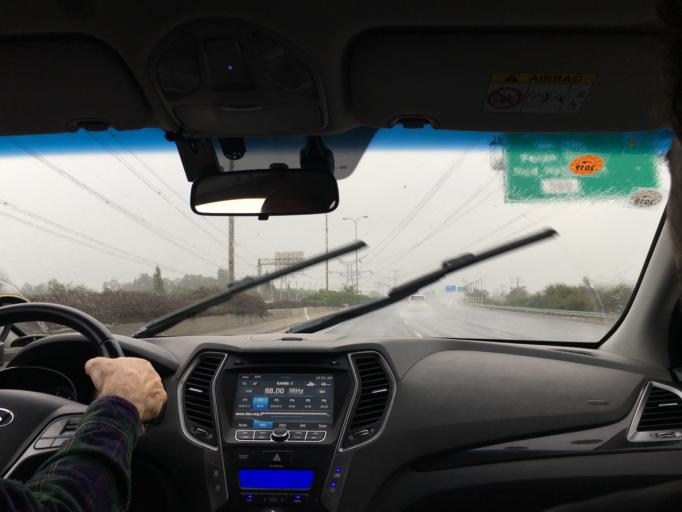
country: IL
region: Central District
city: Petah Tiqwa
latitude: 32.1225
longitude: 34.8933
